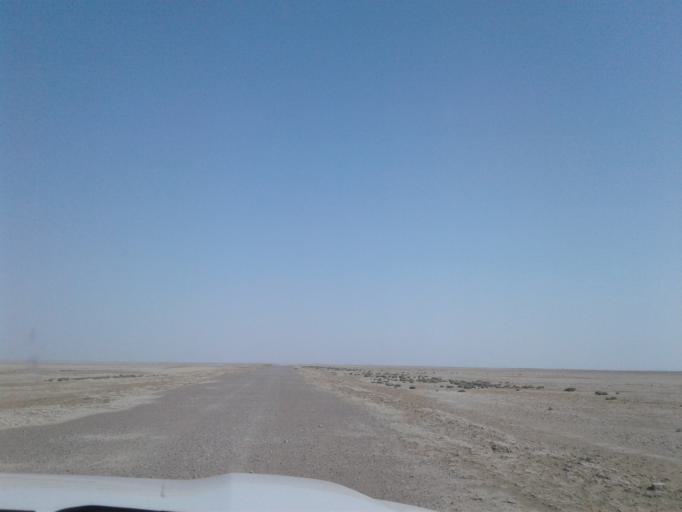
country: TM
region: Balkan
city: Gumdag
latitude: 38.3349
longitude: 54.5662
